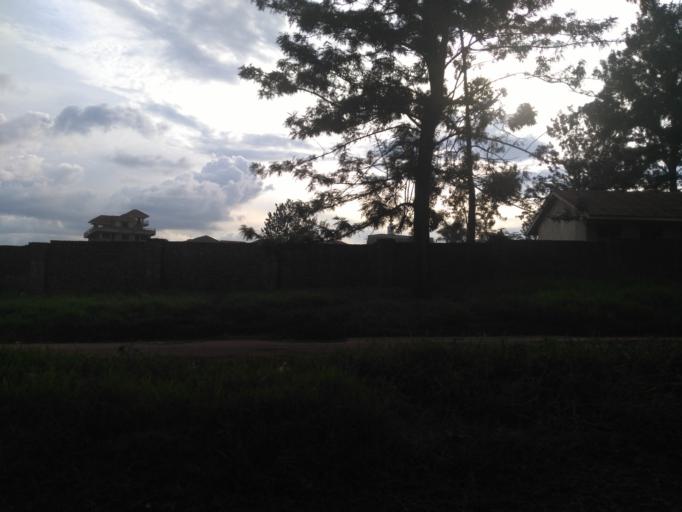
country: UG
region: Eastern Region
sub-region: Jinja District
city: Jinja
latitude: 0.4343
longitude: 33.2141
